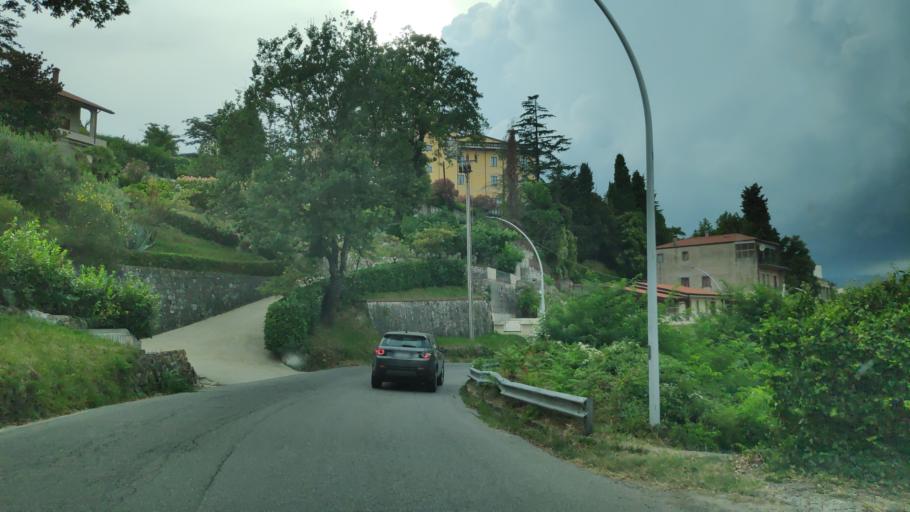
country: IT
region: Calabria
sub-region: Provincia di Catanzaro
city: Chiaravalle Centrale
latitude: 38.6820
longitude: 16.4180
